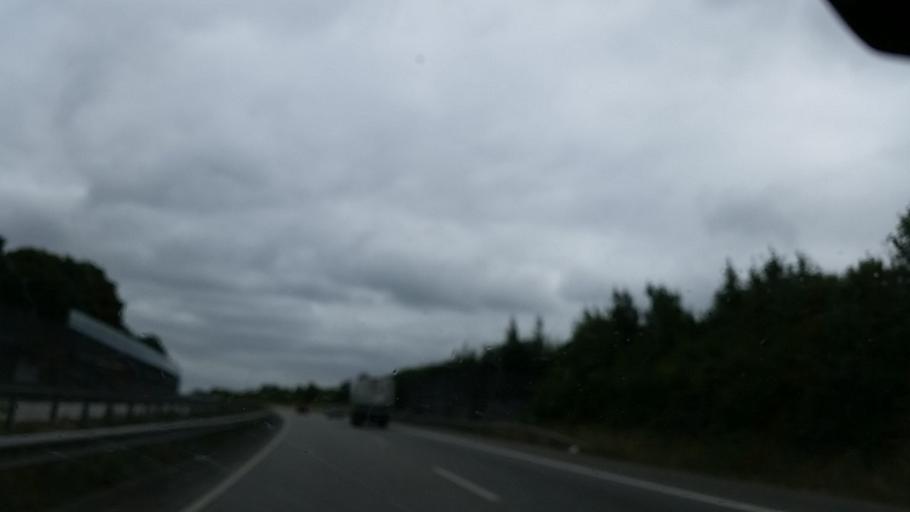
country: DE
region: Schleswig-Holstein
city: Kiel
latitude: 54.2816
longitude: 10.1351
